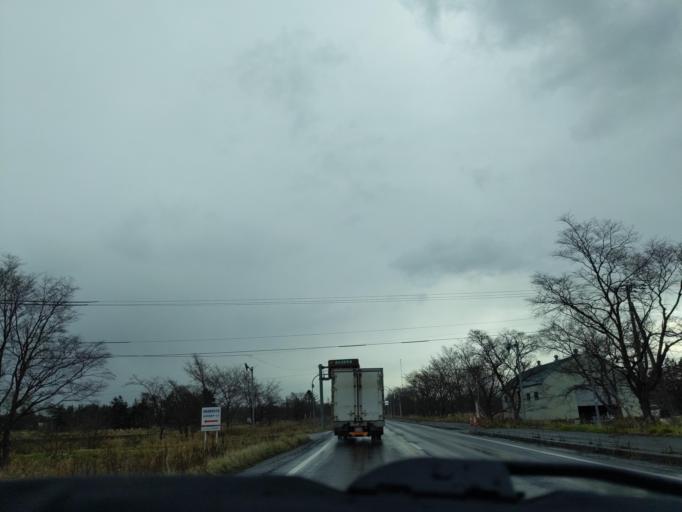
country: JP
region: Hokkaido
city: Ebetsu
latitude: 43.1079
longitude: 141.5937
